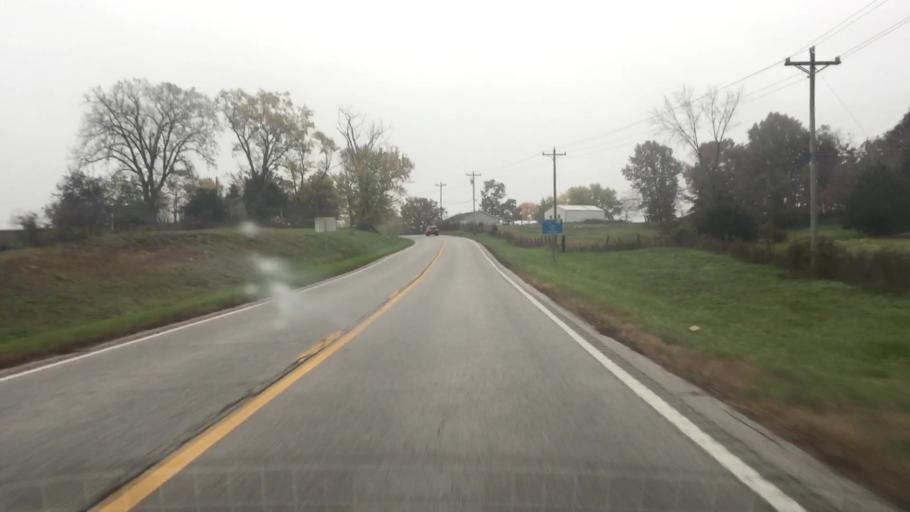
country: US
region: Missouri
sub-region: Callaway County
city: Fulton
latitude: 38.8594
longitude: -91.9987
